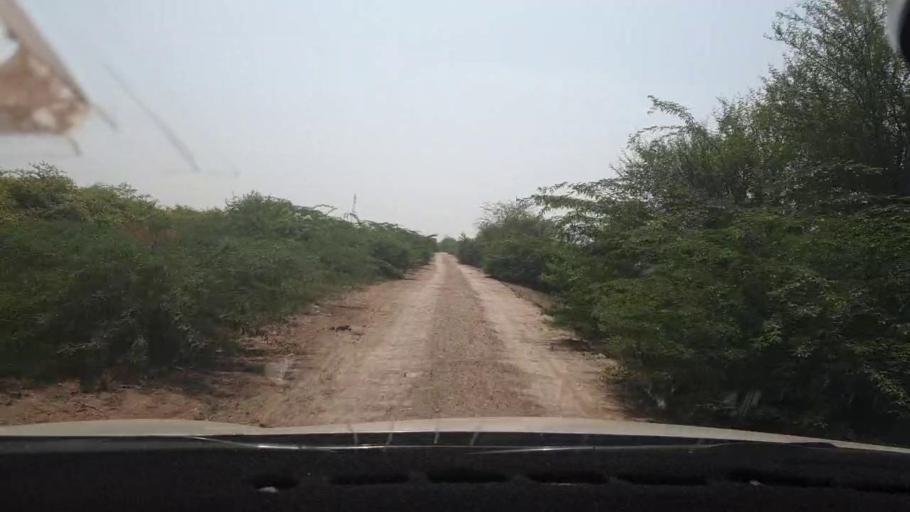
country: PK
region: Sindh
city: Tando Mittha Khan
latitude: 25.9251
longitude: 69.2248
